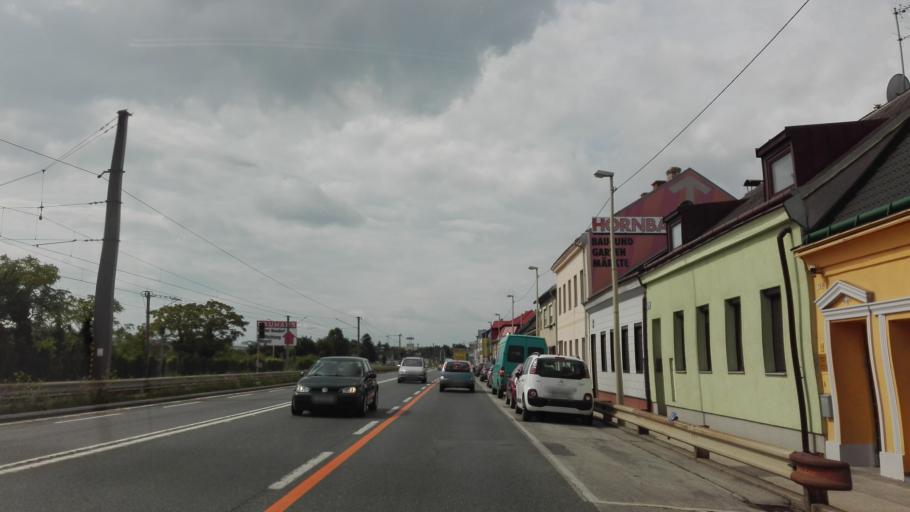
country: AT
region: Lower Austria
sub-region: Politischer Bezirk Modling
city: Vosendorf
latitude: 48.1298
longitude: 16.3213
